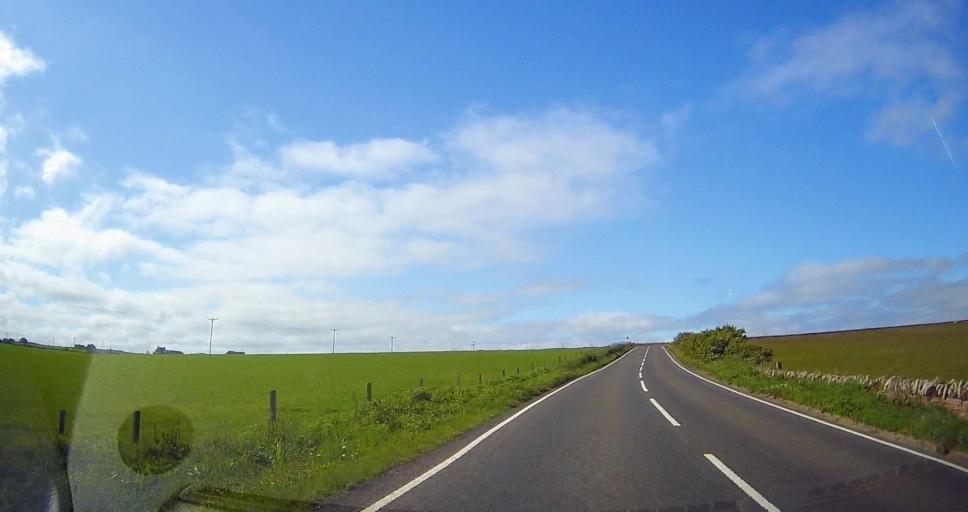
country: GB
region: Scotland
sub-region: Orkney Islands
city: Kirkwall
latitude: 58.9619
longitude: -2.9401
